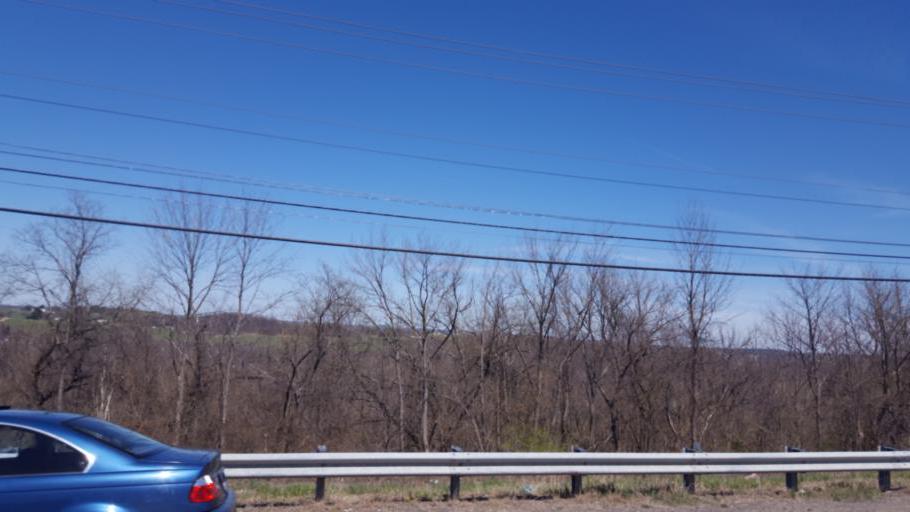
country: US
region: Ohio
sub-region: Belmont County
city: Saint Clairsville
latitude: 40.0721
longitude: -80.8579
